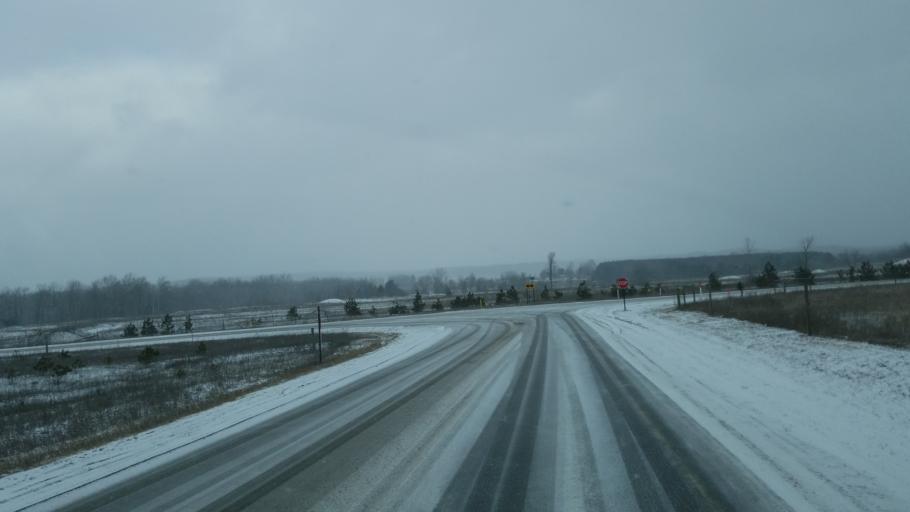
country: US
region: Michigan
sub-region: Osceola County
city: Reed City
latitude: 43.8483
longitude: -85.4241
